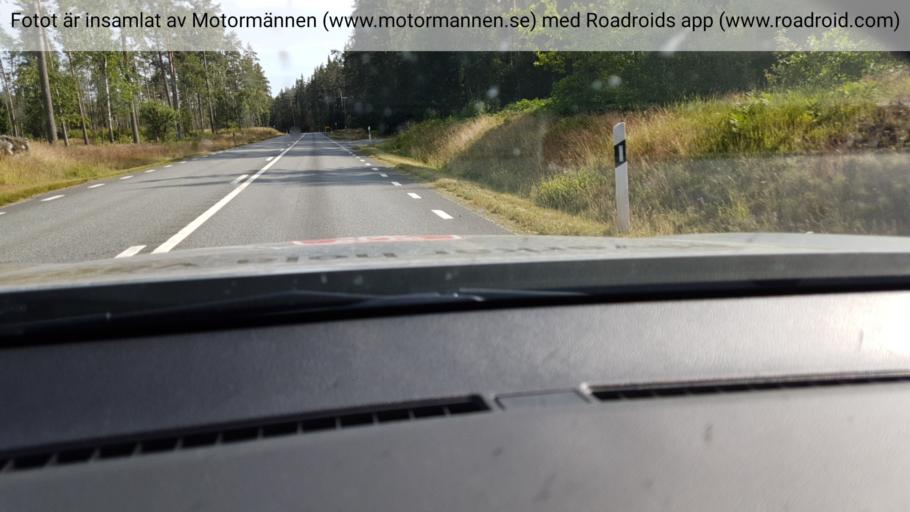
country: SE
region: Joenkoeping
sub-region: Eksjo Kommun
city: Eksjoe
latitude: 57.5918
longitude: 14.9690
